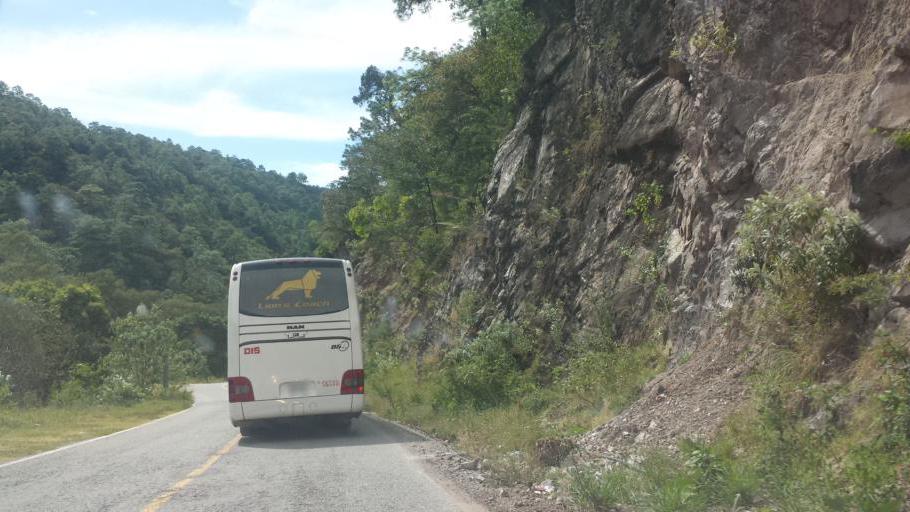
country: MX
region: Oaxaca
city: San Francisco Sola
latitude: 16.4379
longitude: -97.0328
